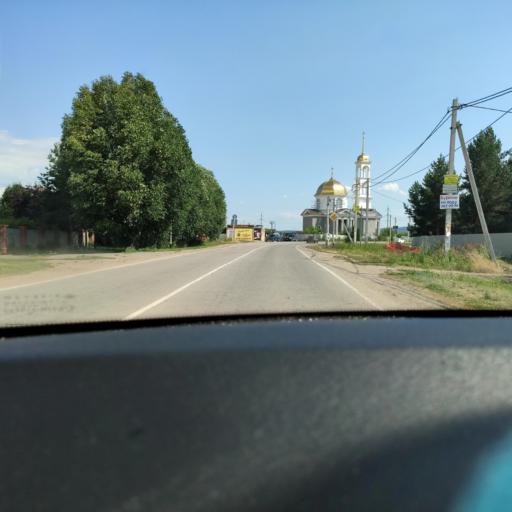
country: RU
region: Samara
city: Volzhskiy
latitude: 53.4491
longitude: 50.1765
